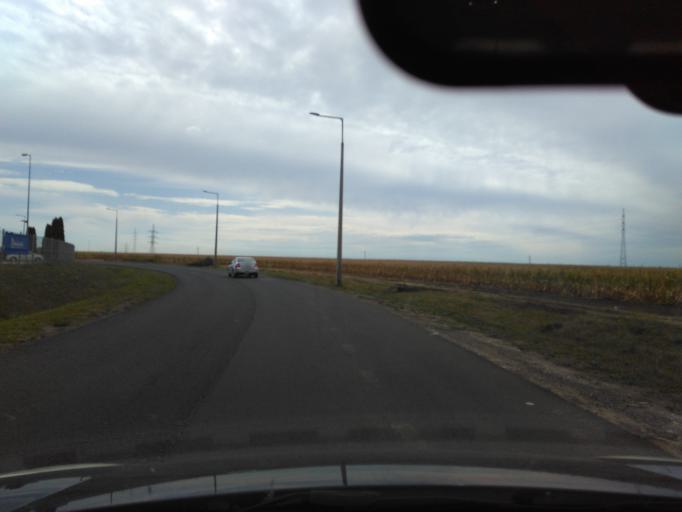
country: HU
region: Heves
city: Hered
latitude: 47.6673
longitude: 19.6421
